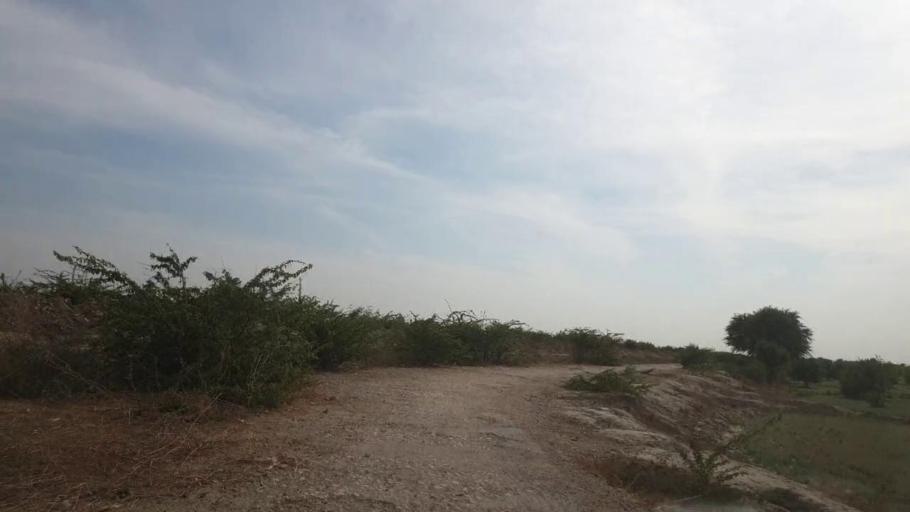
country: PK
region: Sindh
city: Nabisar
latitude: 24.9974
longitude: 69.5593
